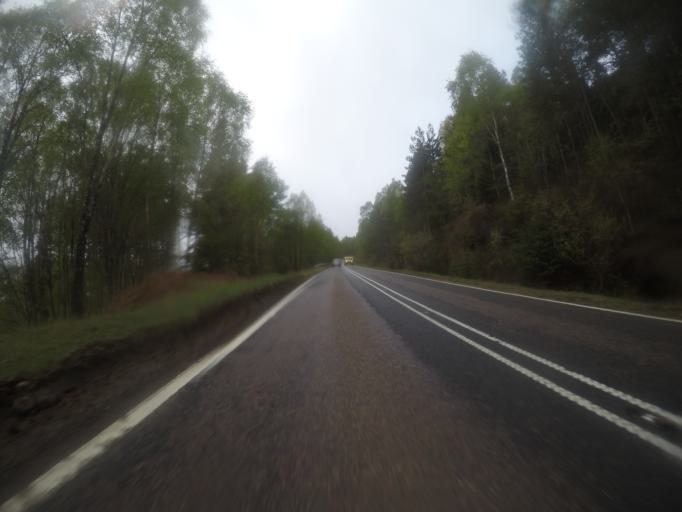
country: GB
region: Scotland
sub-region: Highland
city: Spean Bridge
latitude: 57.0824
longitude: -4.9200
